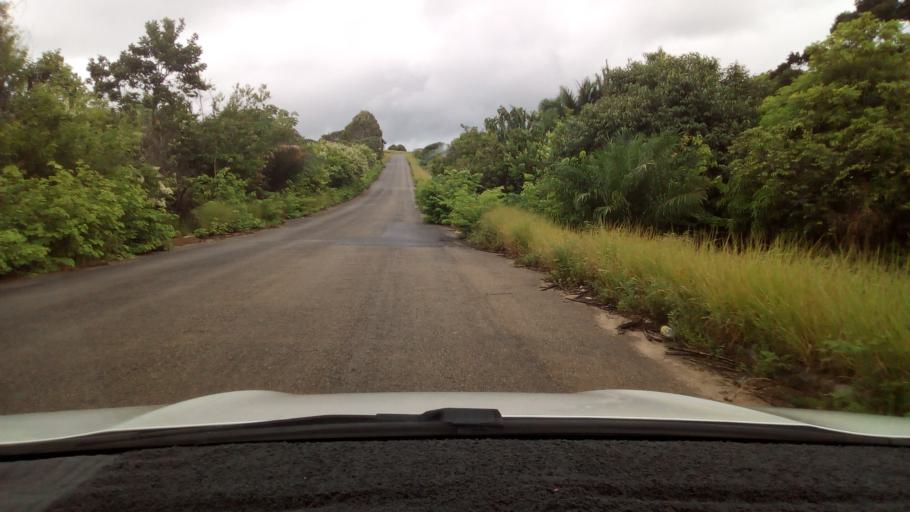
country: BR
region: Paraiba
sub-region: Pitimbu
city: Pitimbu
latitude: -7.3719
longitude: -34.8220
